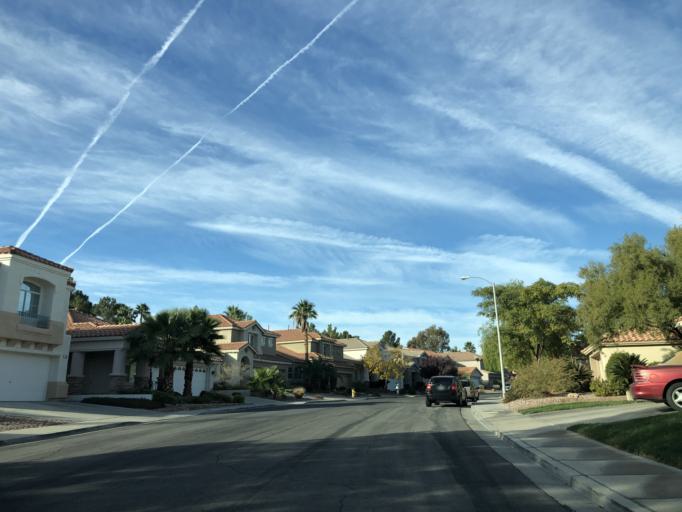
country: US
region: Nevada
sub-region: Clark County
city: Whitney
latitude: 36.0222
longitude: -115.0730
